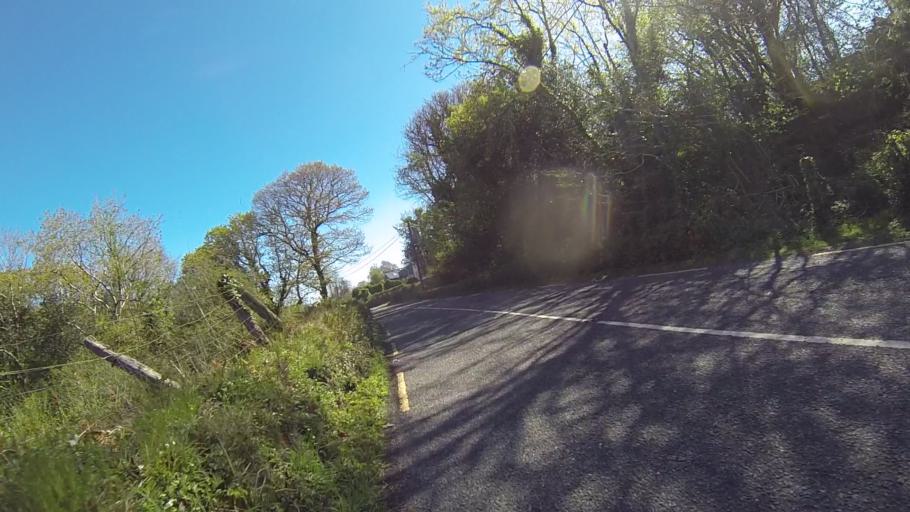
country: IE
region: Munster
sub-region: Ciarrai
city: Kenmare
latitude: 51.8415
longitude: -9.6681
